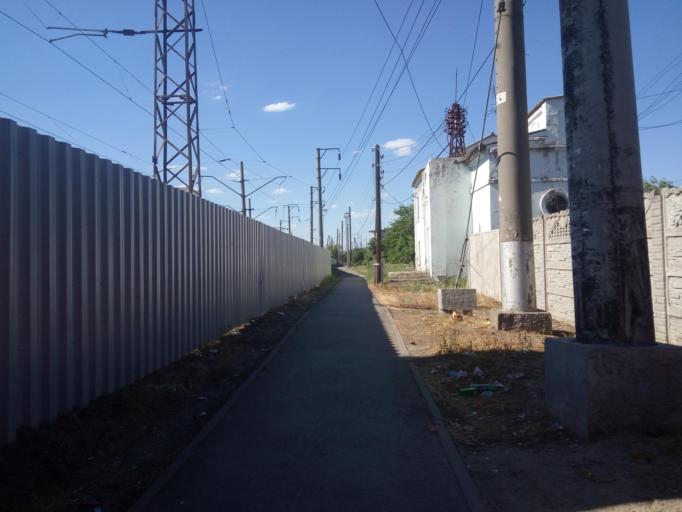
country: RU
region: Rostov
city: Bataysk
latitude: 47.1374
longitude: 39.7587
